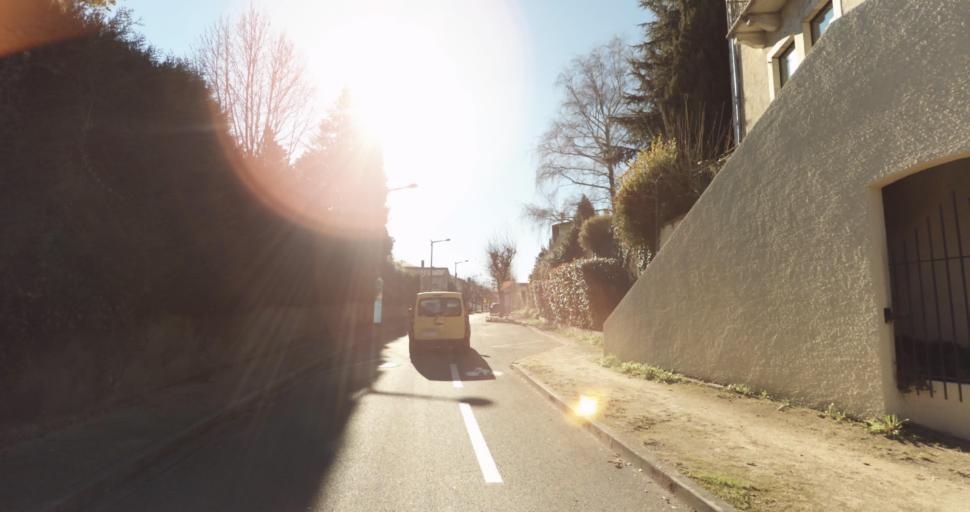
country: FR
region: Aquitaine
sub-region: Departement des Pyrenees-Atlantiques
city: Morlaas
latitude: 43.3467
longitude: -0.2612
